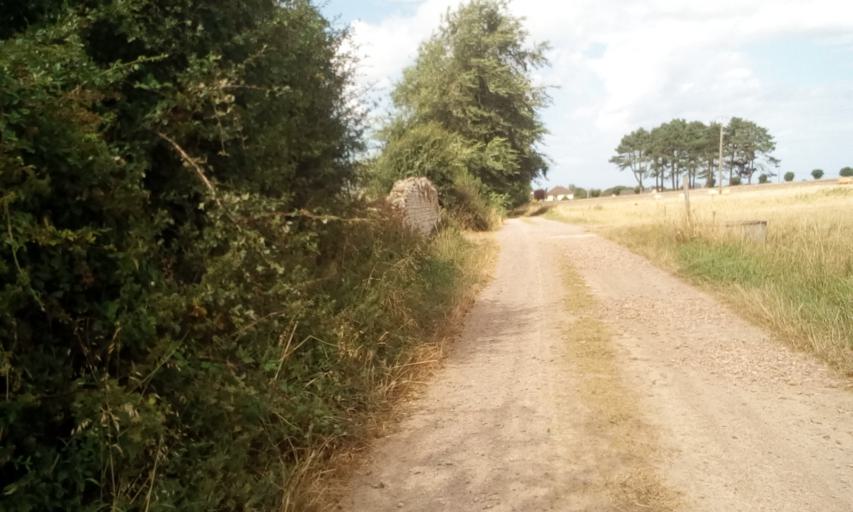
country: FR
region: Lower Normandy
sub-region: Departement du Calvados
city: Ver-sur-Mer
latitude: 49.3276
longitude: -0.5279
